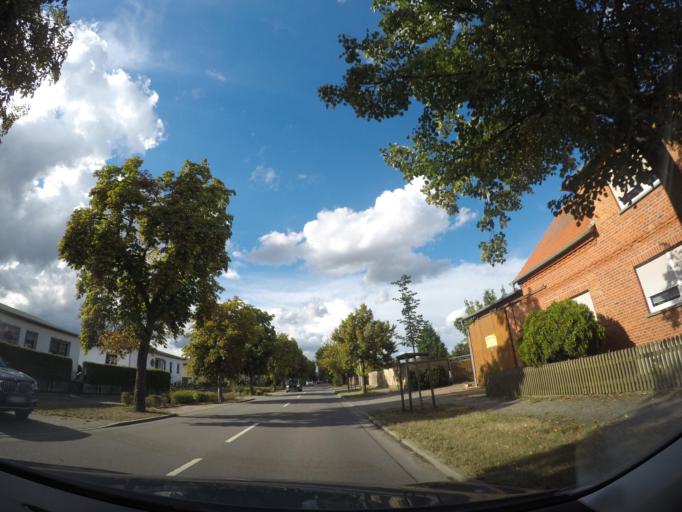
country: DE
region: Saxony-Anhalt
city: Bulstringen
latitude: 52.3173
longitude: 11.3496
